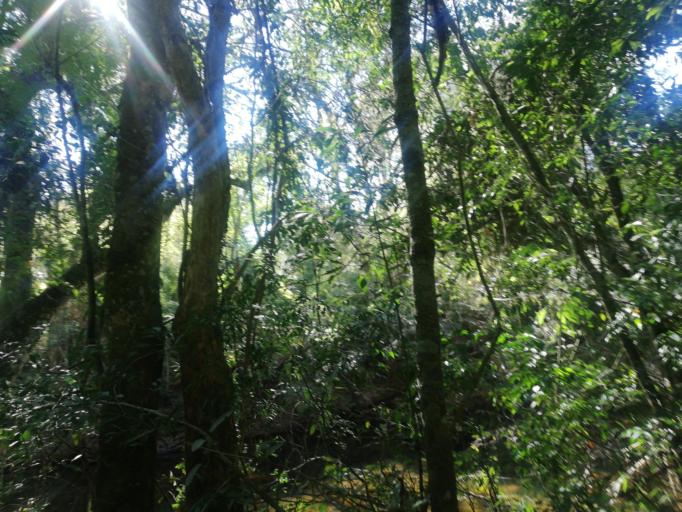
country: AR
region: Misiones
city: Colonia Wanda
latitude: -25.8573
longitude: -54.1664
